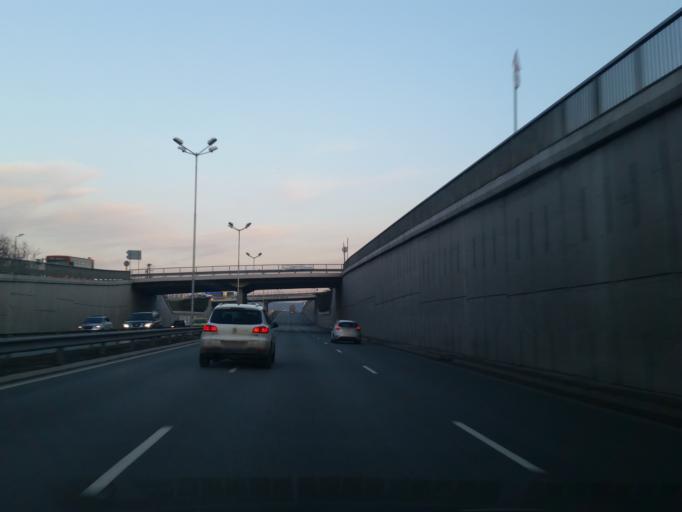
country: BG
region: Sofia-Capital
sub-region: Stolichna Obshtina
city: Sofia
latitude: 42.6422
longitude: 23.3109
